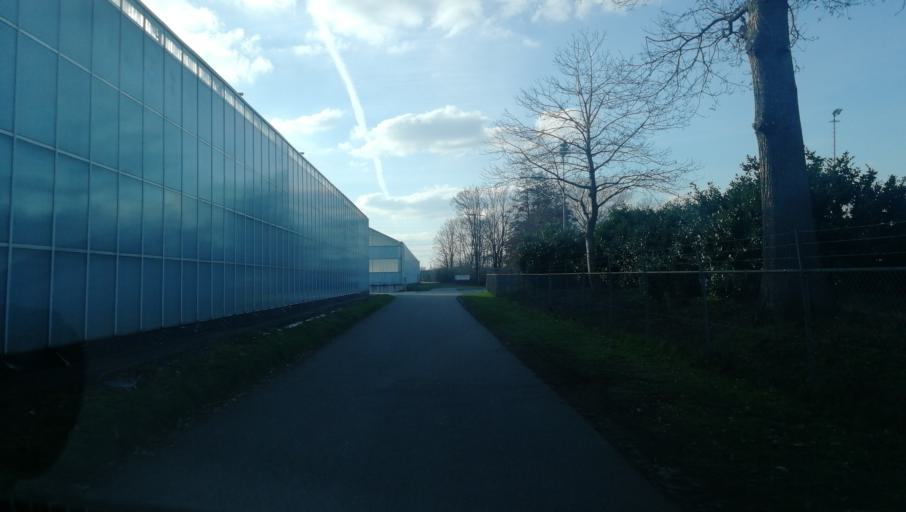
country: NL
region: Limburg
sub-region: Gemeente Venlo
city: Tegelen
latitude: 51.3438
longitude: 6.1023
